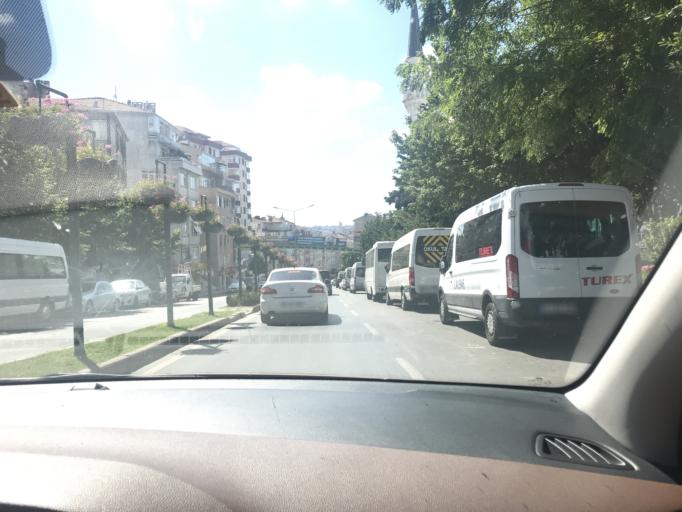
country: TR
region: Istanbul
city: UEskuedar
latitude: 41.0164
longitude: 29.0252
